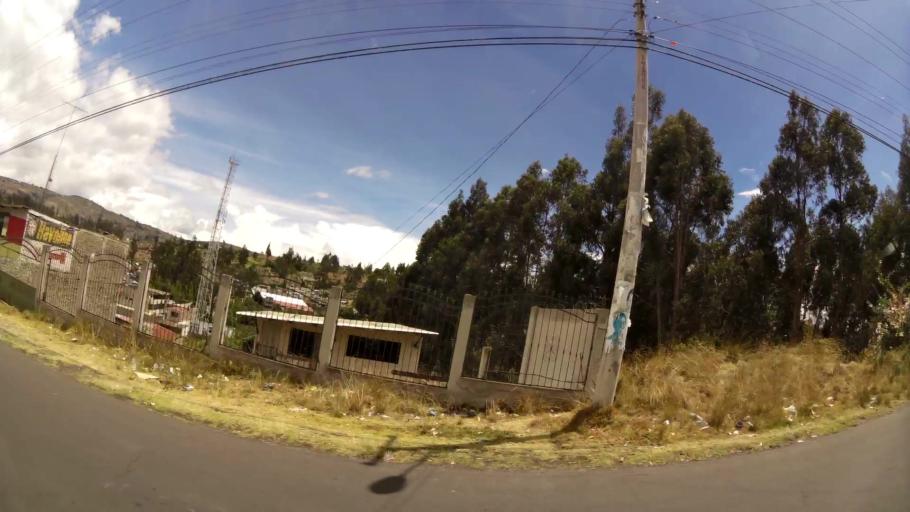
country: EC
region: Tungurahua
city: Ambato
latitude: -1.2743
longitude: -78.5879
